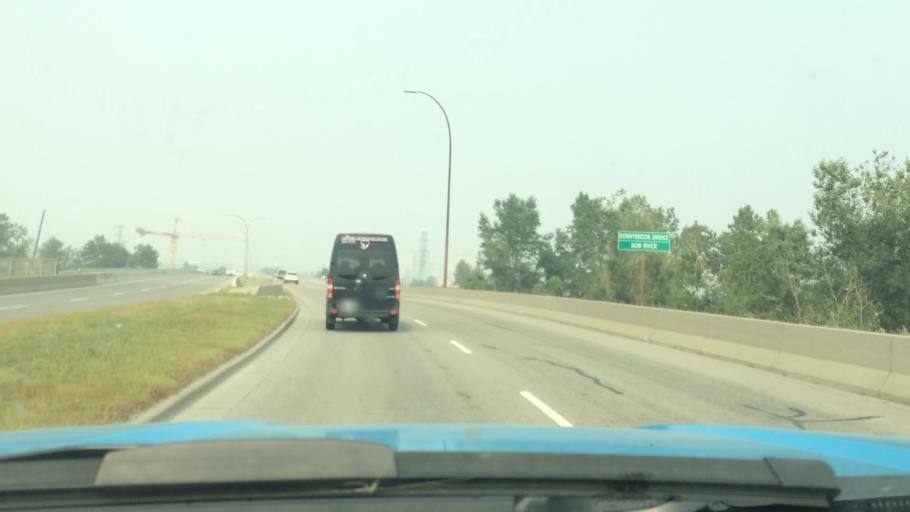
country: CA
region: Alberta
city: Calgary
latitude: 51.0120
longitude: -114.0113
